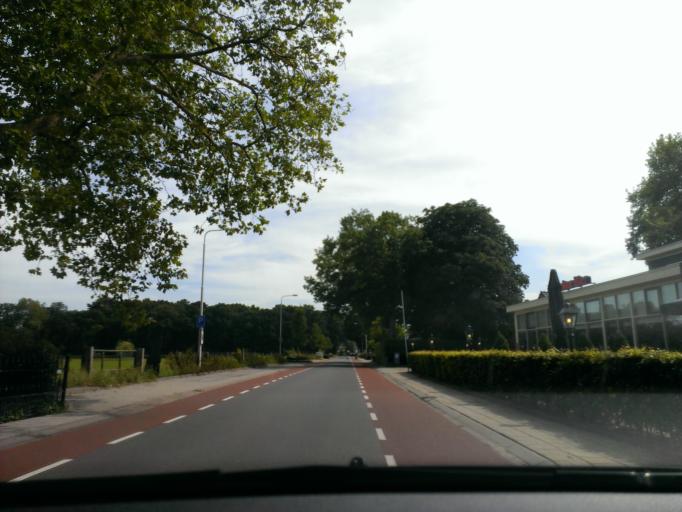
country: NL
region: Gelderland
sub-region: Gemeente Voorst
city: Twello
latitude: 52.2814
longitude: 6.1004
